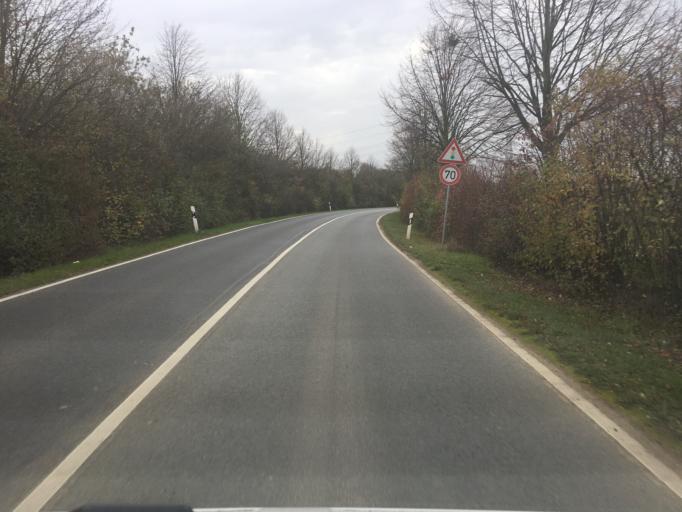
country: DE
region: North Rhine-Westphalia
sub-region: Regierungsbezirk Koln
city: Hurth
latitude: 50.8969
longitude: 6.8849
